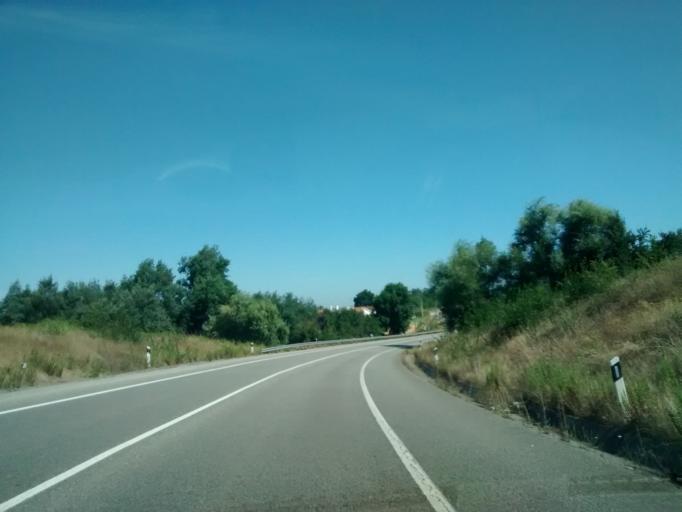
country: PT
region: Aveiro
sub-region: Anadia
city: Sangalhos
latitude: 40.4876
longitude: -8.4820
